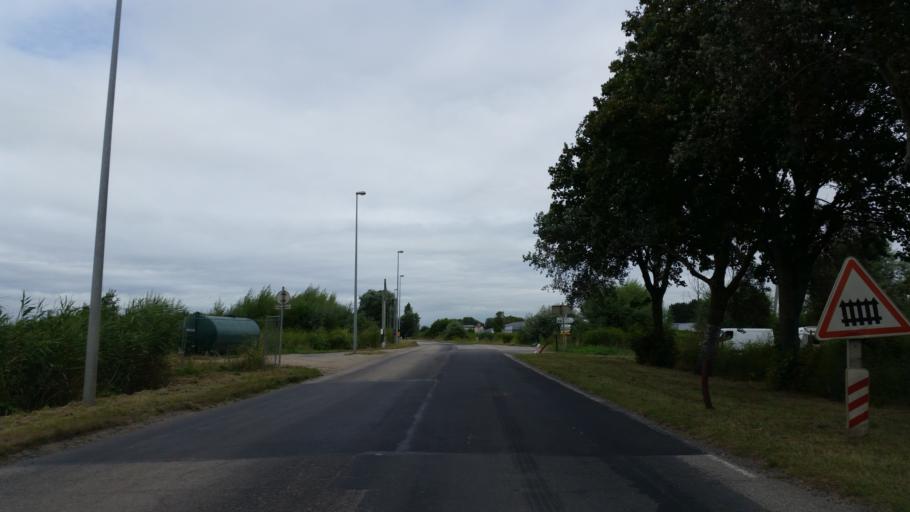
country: FR
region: Lower Normandy
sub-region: Departement du Calvados
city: La Riviere-Saint-Sauveur
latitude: 49.4196
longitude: 0.2599
